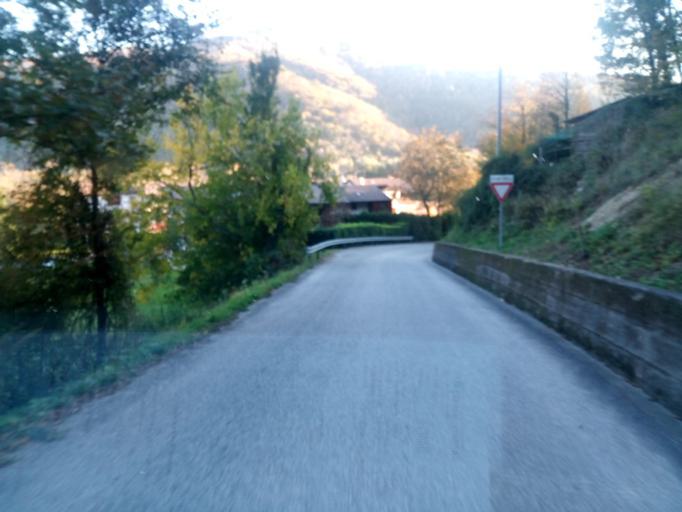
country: IT
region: Friuli Venezia Giulia
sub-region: Provincia di Udine
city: Merso di Sopra
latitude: 46.1188
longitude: 13.5110
